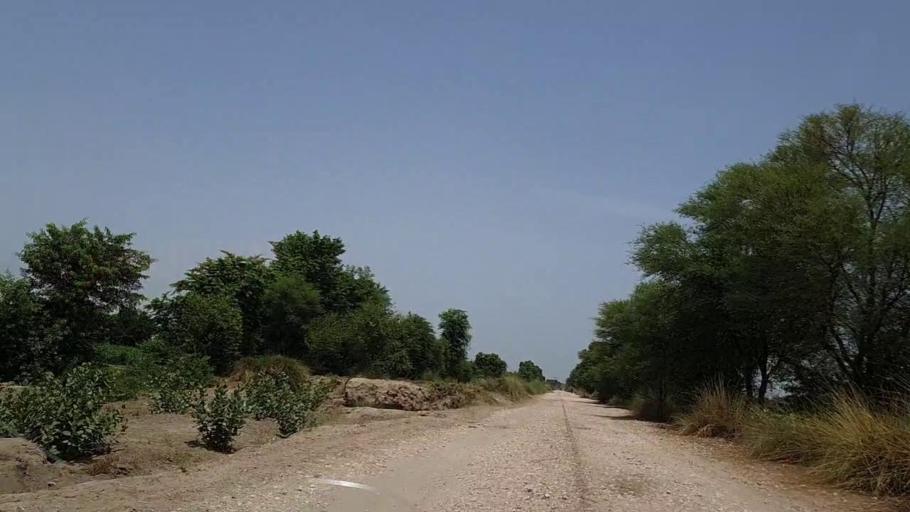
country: PK
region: Sindh
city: Tharu Shah
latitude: 26.9153
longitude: 68.0019
